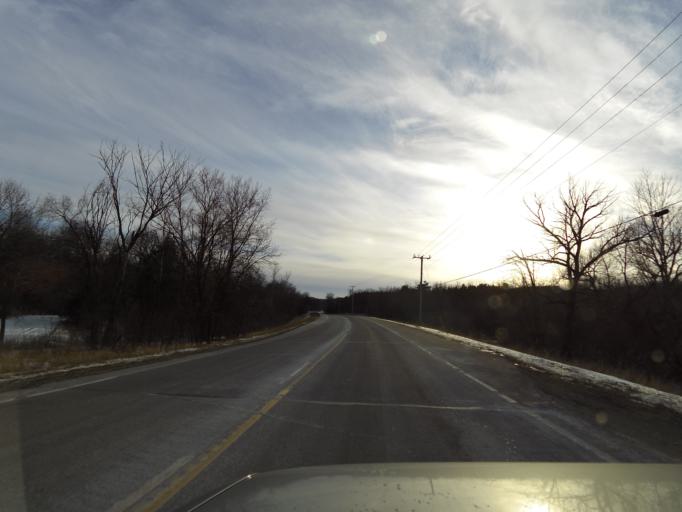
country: US
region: Minnesota
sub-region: Washington County
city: Afton
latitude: 44.9128
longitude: -92.7792
